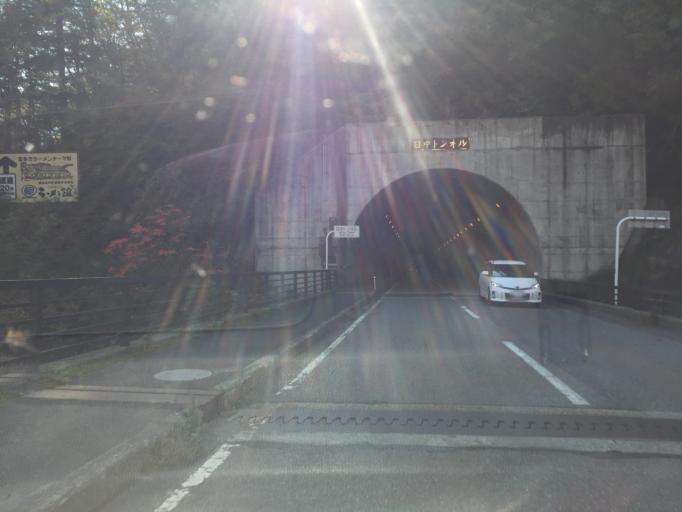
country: JP
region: Fukushima
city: Kitakata
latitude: 37.7616
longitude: 139.9125
